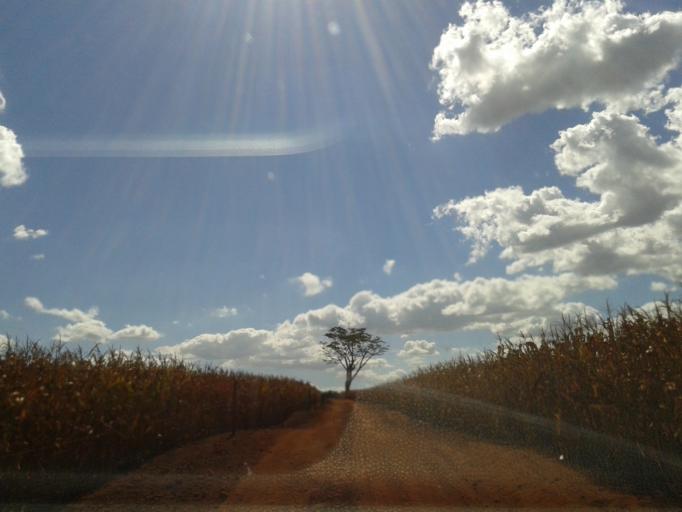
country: BR
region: Minas Gerais
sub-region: Capinopolis
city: Capinopolis
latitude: -18.6239
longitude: -49.4733
